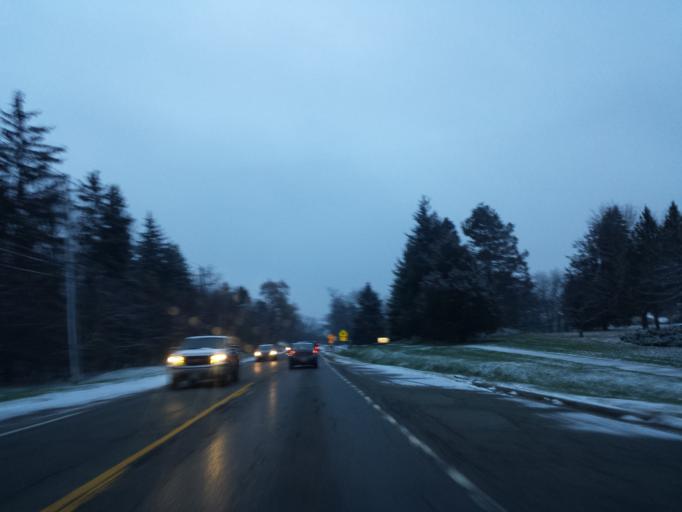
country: US
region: Michigan
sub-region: Oakland County
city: Sylvan Lake
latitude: 42.5832
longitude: -83.3301
